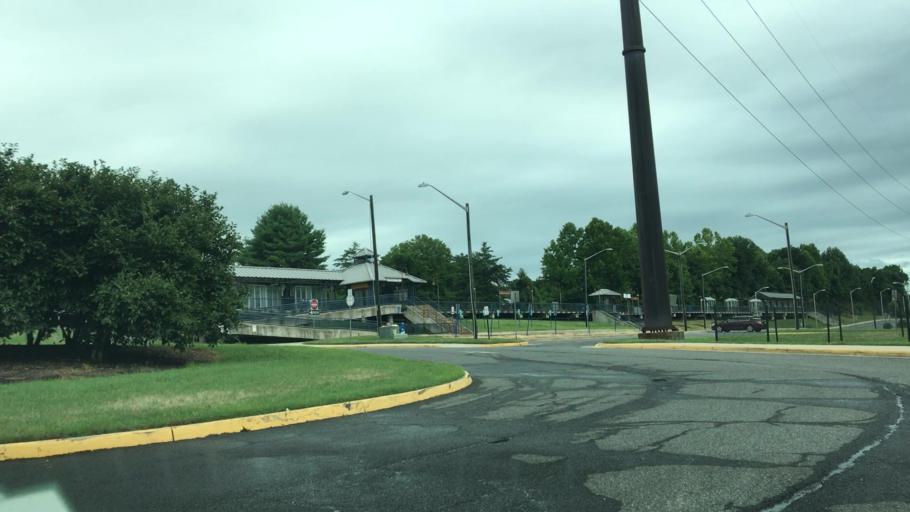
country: US
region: Virginia
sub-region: Prince William County
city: Yorkshire
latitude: 38.7648
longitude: -77.4407
